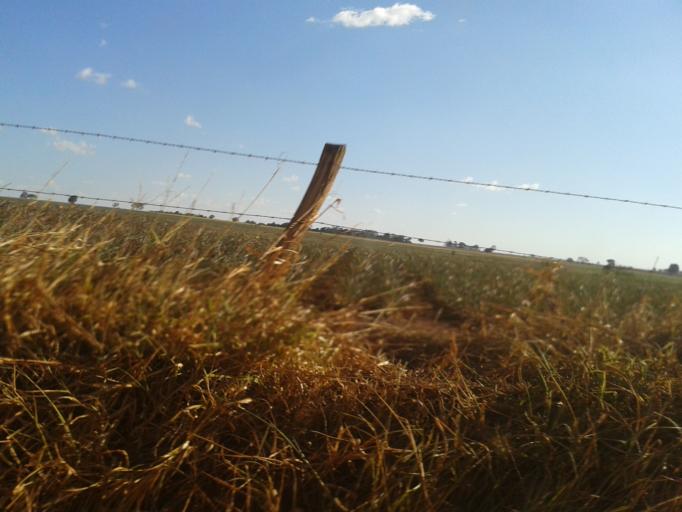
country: BR
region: Minas Gerais
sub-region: Centralina
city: Centralina
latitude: -18.7420
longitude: -49.1895
